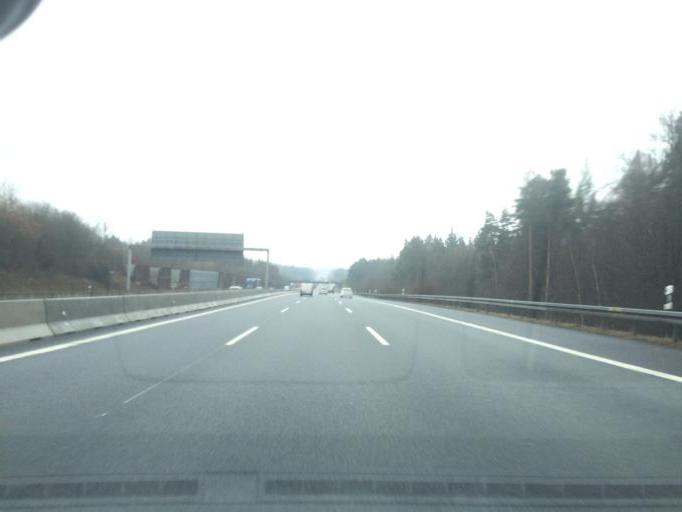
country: DE
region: Bavaria
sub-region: Regierungsbezirk Mittelfranken
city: Schnaittach
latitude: 49.5576
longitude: 11.3243
